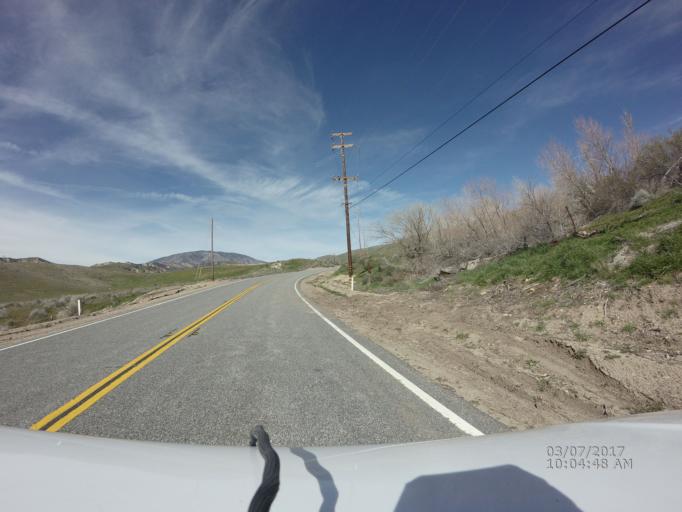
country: US
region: California
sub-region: Kern County
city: Lebec
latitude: 34.7813
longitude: -118.8044
